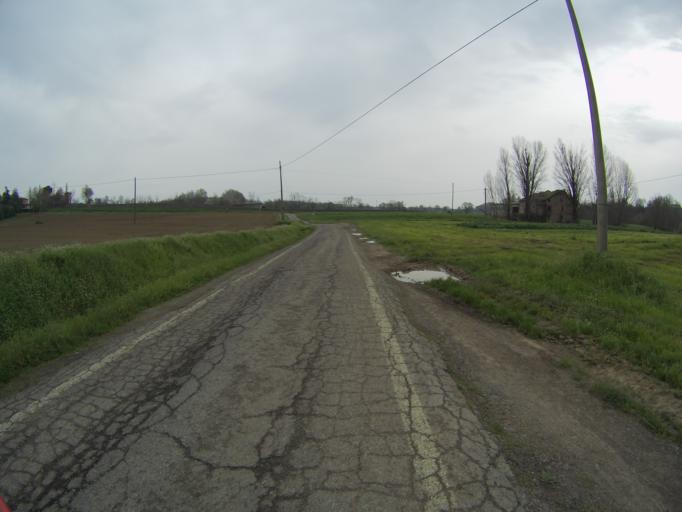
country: IT
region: Emilia-Romagna
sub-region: Provincia di Reggio Emilia
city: Barco
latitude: 44.6593
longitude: 10.5096
